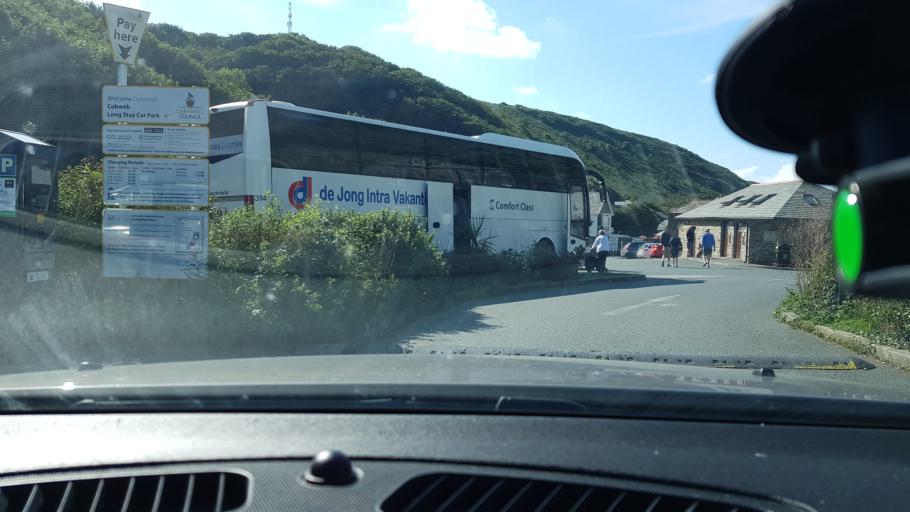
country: GB
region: England
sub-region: Cornwall
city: Tintagel
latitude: 50.6897
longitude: -4.6907
